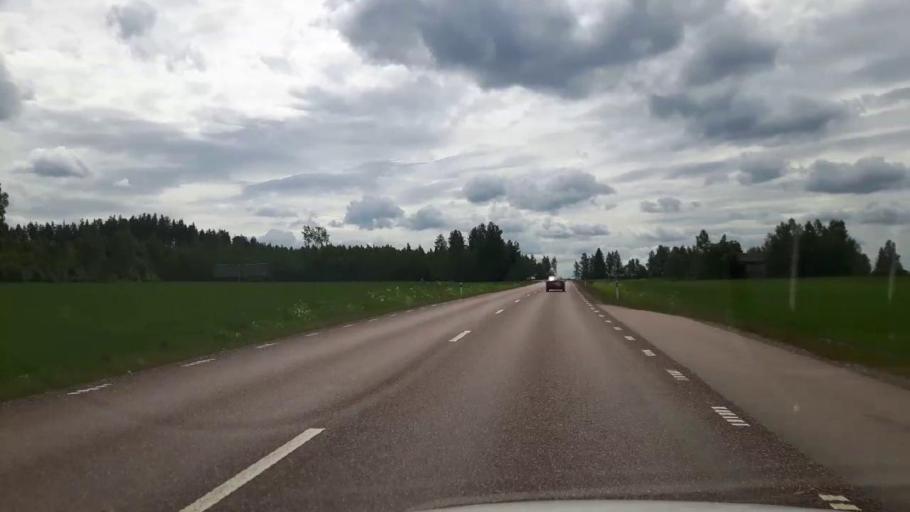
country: SE
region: Dalarna
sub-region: Hedemora Kommun
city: Hedemora
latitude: 60.3403
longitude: 15.9455
